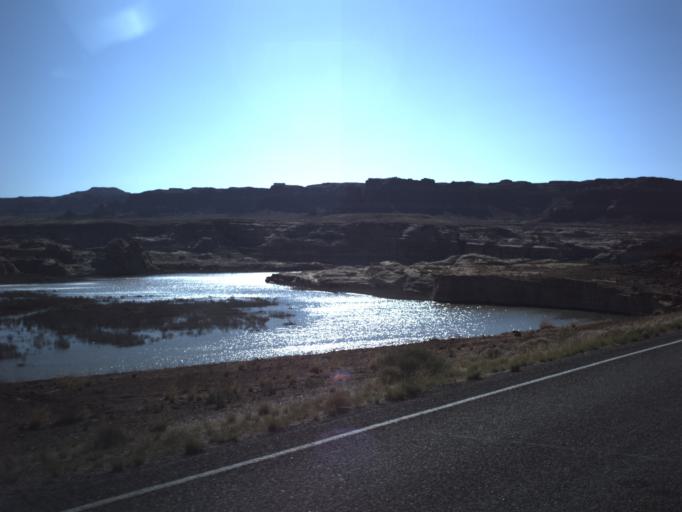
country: US
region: Utah
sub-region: San Juan County
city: Blanding
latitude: 37.8966
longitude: -110.3982
